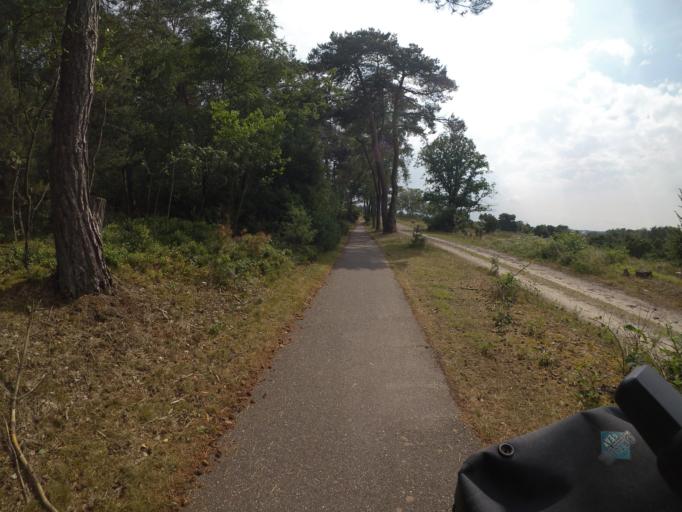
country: NL
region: Overijssel
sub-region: Gemeente Twenterand
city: Den Ham
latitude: 52.4761
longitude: 6.4007
